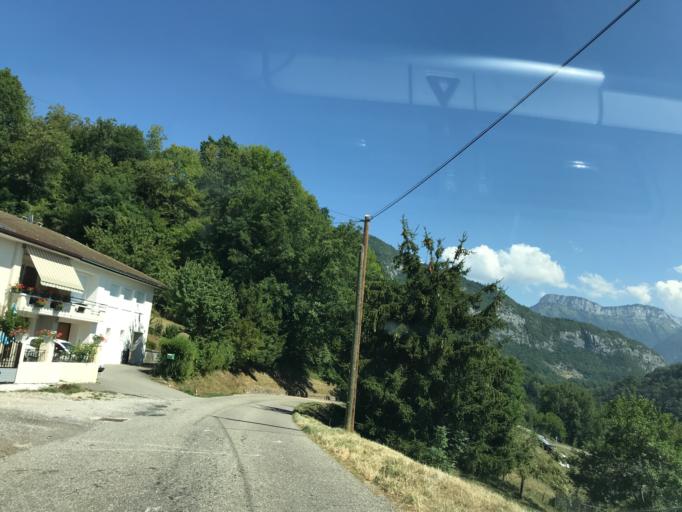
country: FR
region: Rhone-Alpes
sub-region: Departement de la Haute-Savoie
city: Villaz
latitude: 45.9281
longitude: 6.1855
